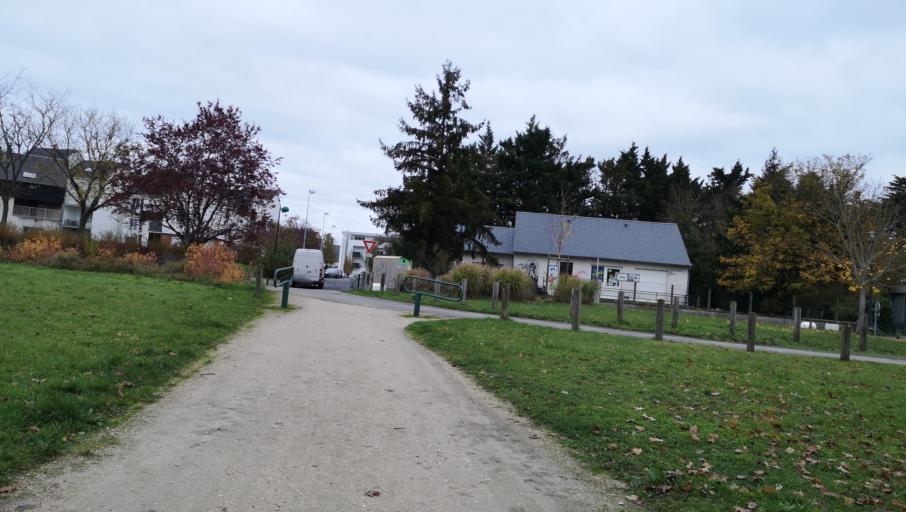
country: FR
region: Centre
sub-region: Departement du Loiret
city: Saint-Jean-de-Braye
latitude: 47.9127
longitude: 1.9703
